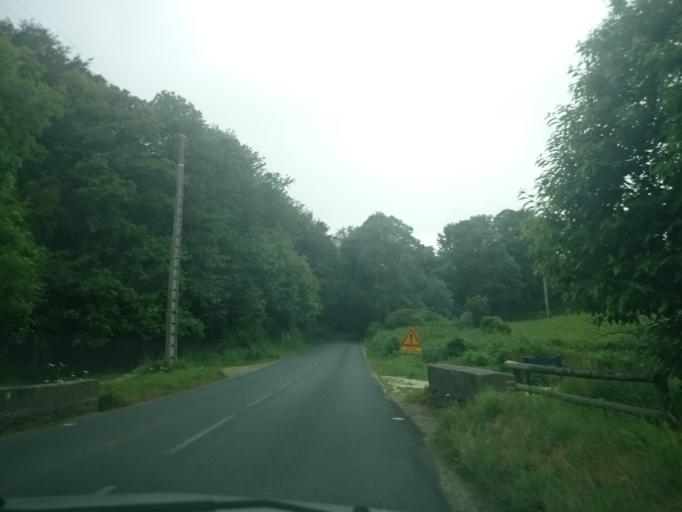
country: FR
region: Brittany
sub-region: Departement du Finistere
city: Saint-Pabu
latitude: 48.5533
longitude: -4.5952
